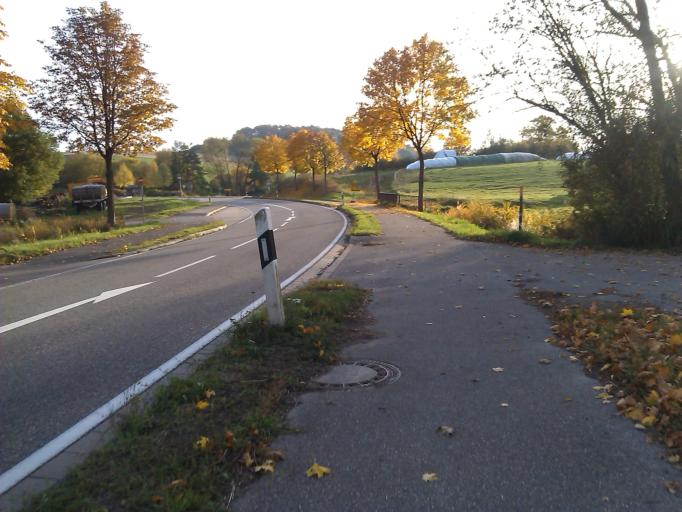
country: DE
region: Rheinland-Pfalz
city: Niederkirchen
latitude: 49.5620
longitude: 7.6882
